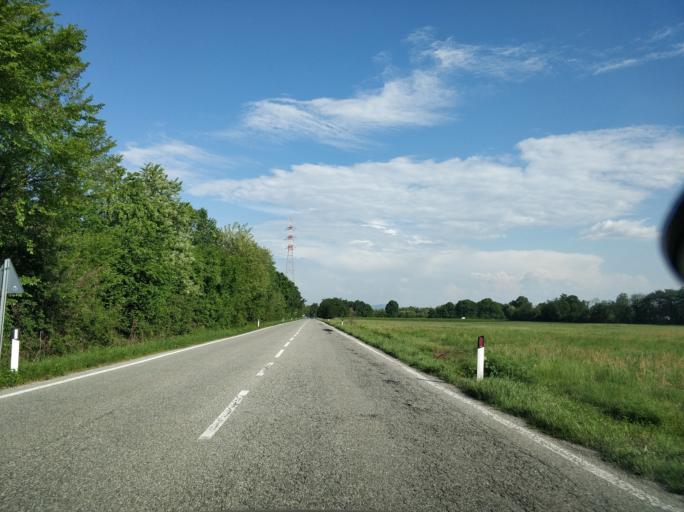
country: IT
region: Piedmont
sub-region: Provincia di Torino
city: Villanova Canavese
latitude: 45.2394
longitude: 7.5381
